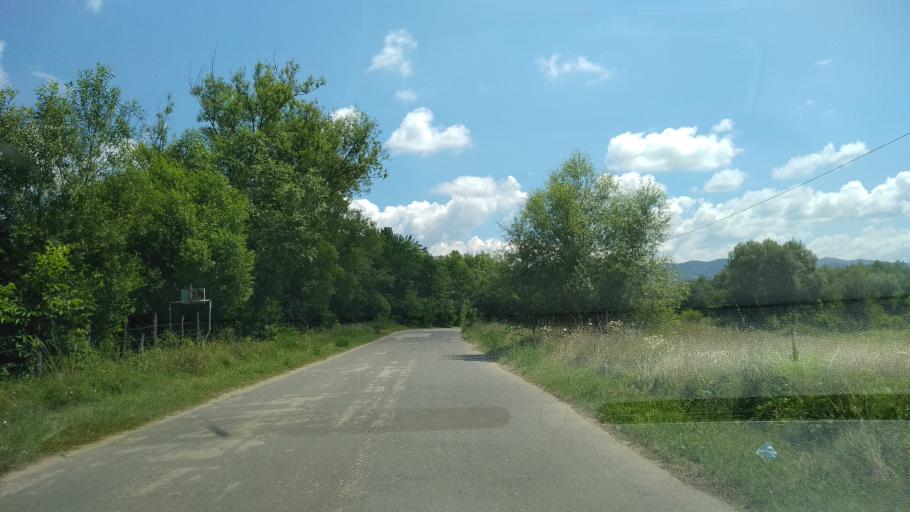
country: RO
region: Hunedoara
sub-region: Comuna Bosorod
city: Bosorod
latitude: 45.7034
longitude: 23.0737
